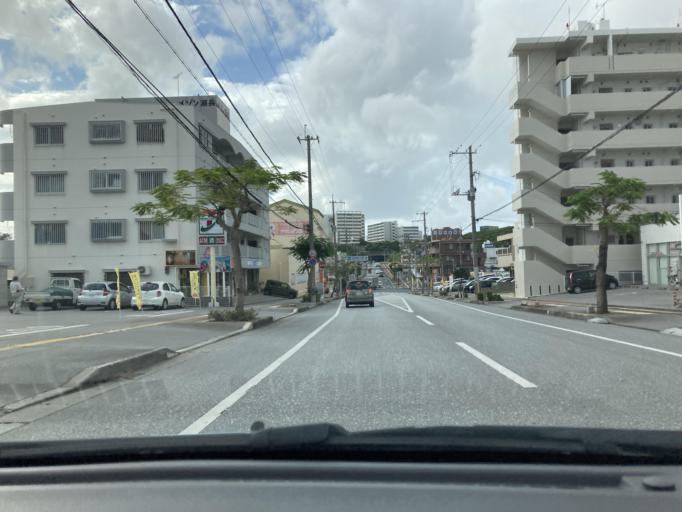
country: JP
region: Okinawa
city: Tomigusuku
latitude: 26.1833
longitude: 127.6773
